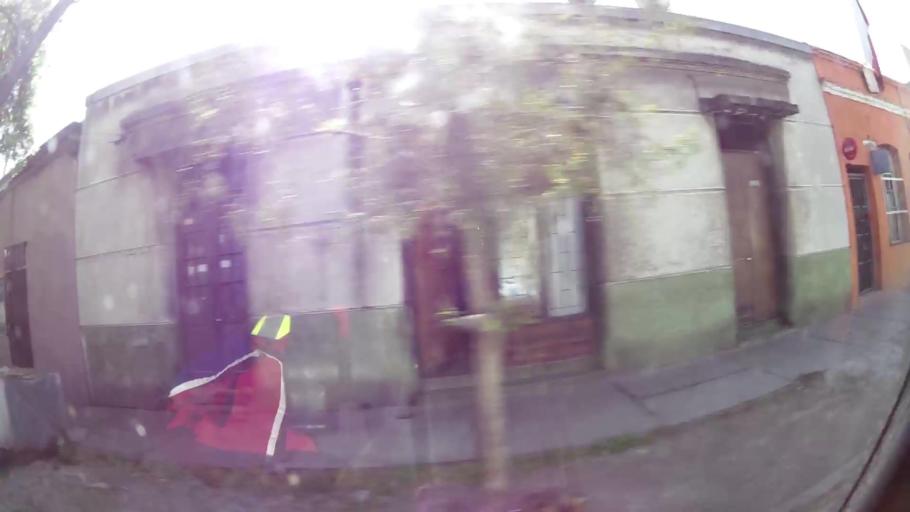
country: CL
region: Santiago Metropolitan
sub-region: Provincia de Santiago
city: Santiago
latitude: -33.4779
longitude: -70.6573
